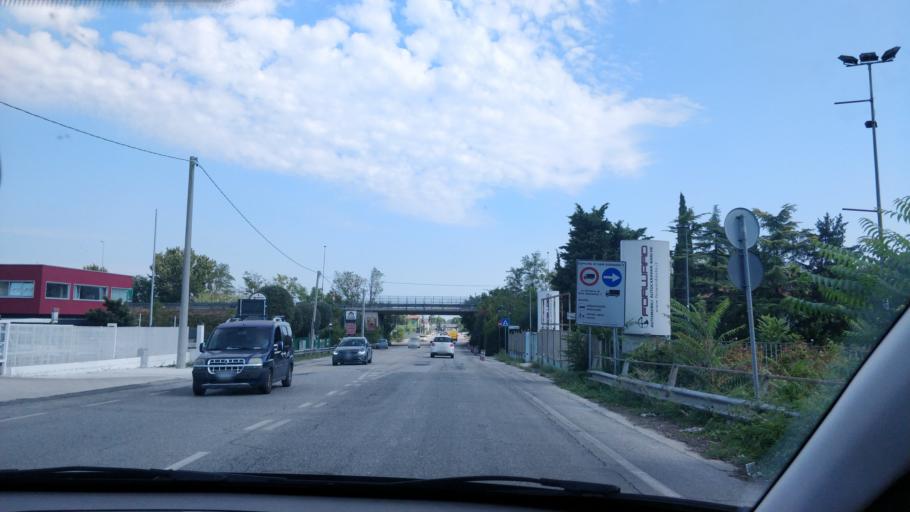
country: IT
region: Abruzzo
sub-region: Provincia di Chieti
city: Chieti
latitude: 42.3936
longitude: 14.1615
